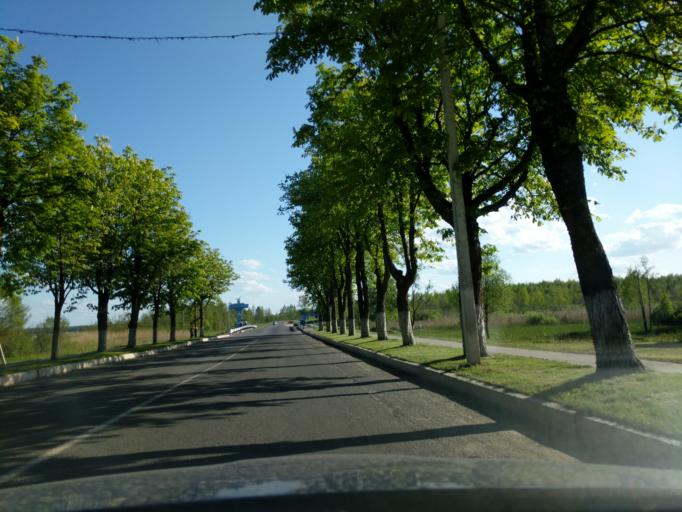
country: BY
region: Minsk
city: Myadzyel
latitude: 54.8650
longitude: 26.9334
